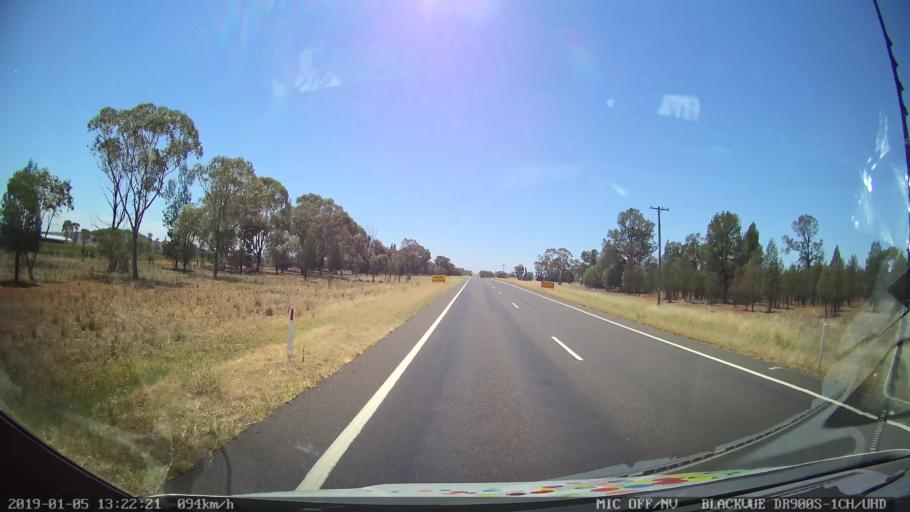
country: AU
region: New South Wales
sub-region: Gunnedah
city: Gunnedah
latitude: -31.0869
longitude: 149.9607
